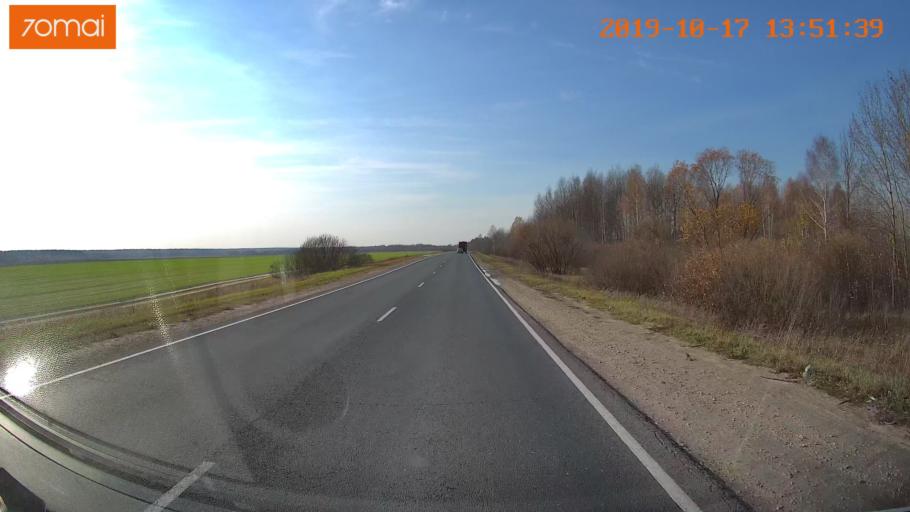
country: RU
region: Rjazan
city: Tuma
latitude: 55.1398
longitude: 40.3836
